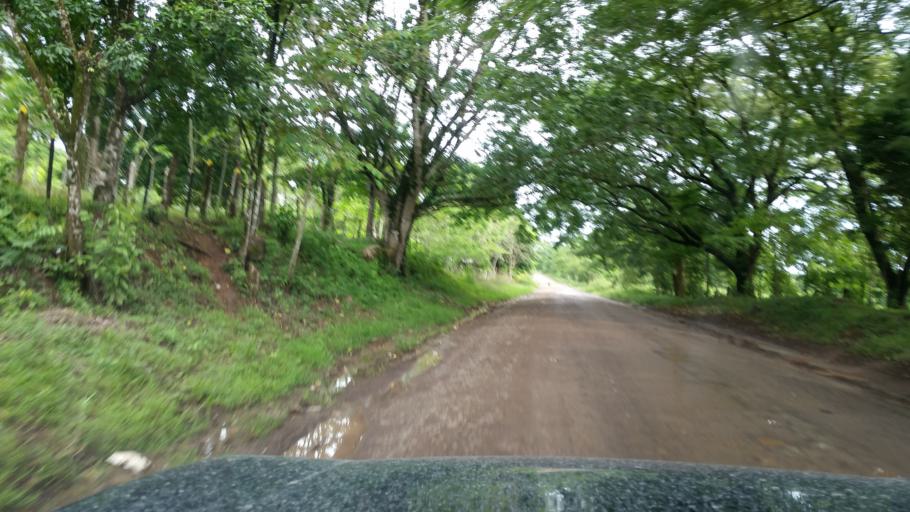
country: NI
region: Atlantico Norte (RAAN)
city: Siuna
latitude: 13.4265
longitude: -84.8527
